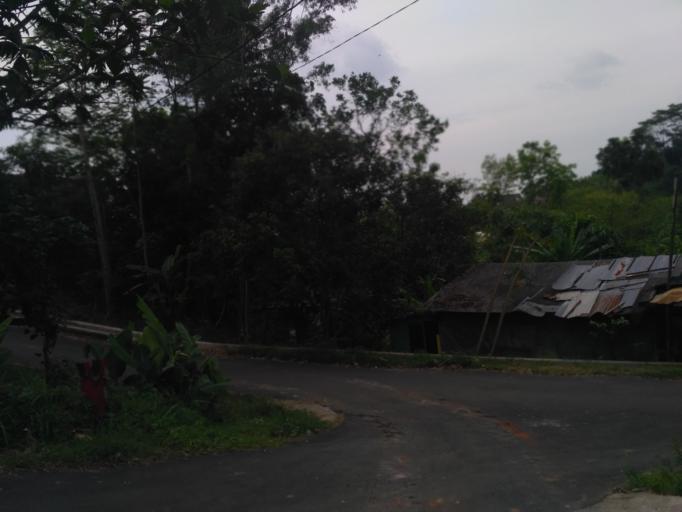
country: ID
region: Central Java
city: Ungaran
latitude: -7.0812
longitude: 110.4268
